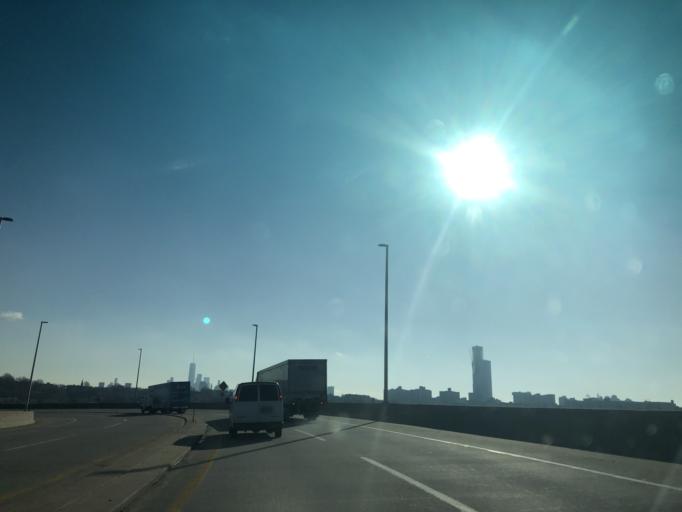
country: US
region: New Jersey
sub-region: Hudson County
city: Jersey City
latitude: 40.7508
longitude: -74.0701
